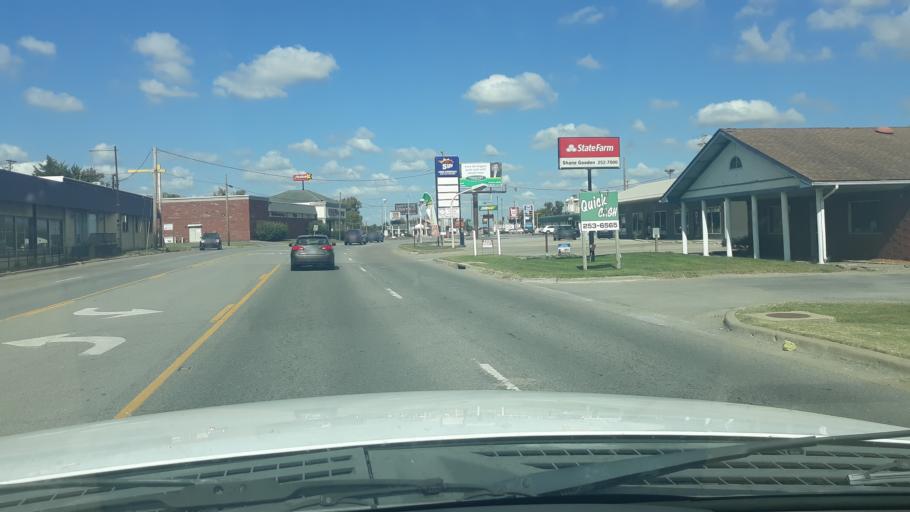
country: US
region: Illinois
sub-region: Saline County
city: Harrisburg
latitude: 37.7361
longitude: -88.5332
